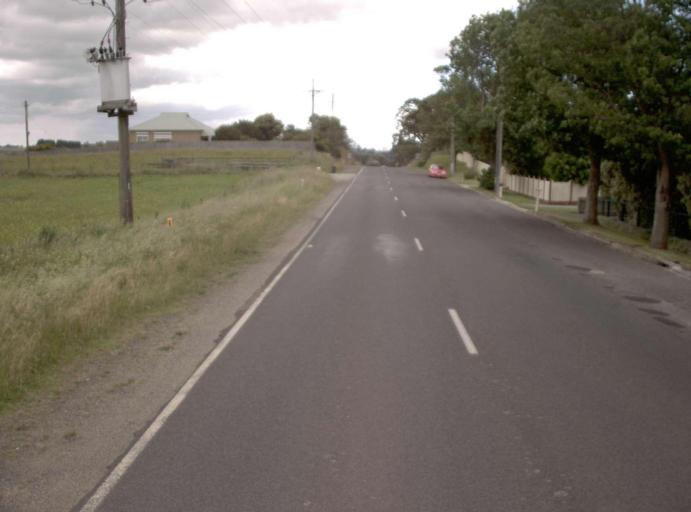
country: AU
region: Victoria
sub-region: Baw Baw
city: Warragul
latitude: -38.1367
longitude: 145.9351
